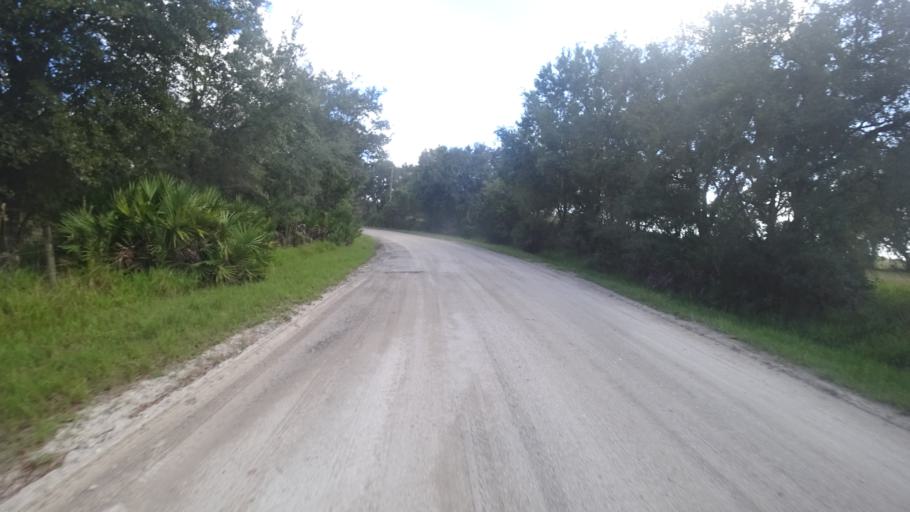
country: US
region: Florida
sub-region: Sarasota County
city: Lake Sarasota
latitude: 27.4239
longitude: -82.1447
